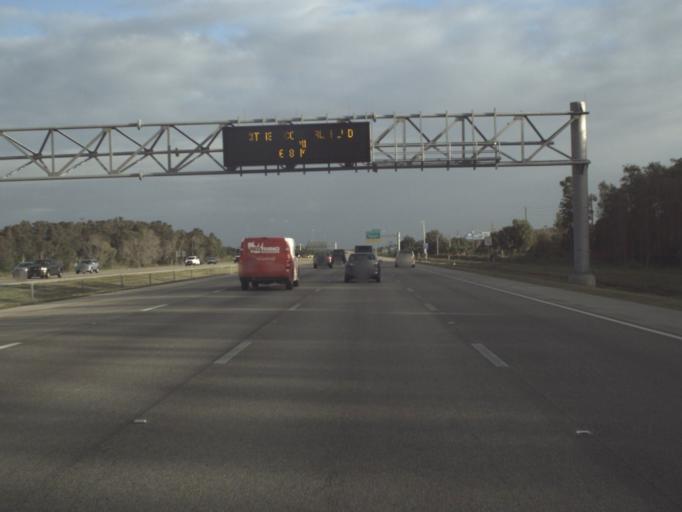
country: US
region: Florida
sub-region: Lee County
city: Three Oaks
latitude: 26.5312
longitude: -81.7947
